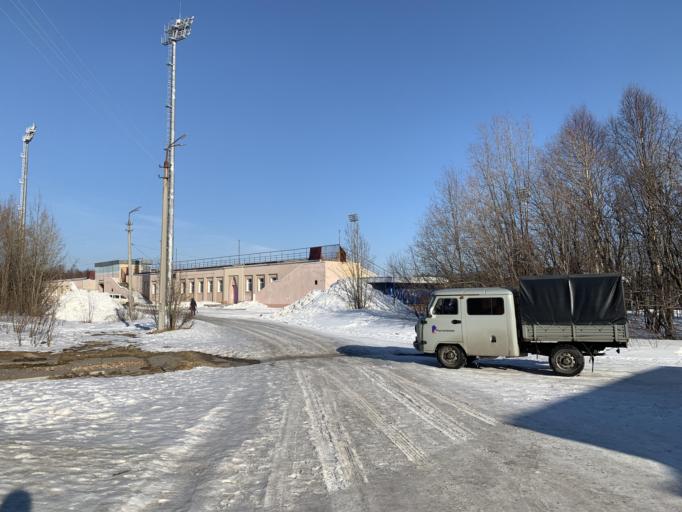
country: RU
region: Murmansk
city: Monchegorsk
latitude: 67.9401
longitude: 32.9406
